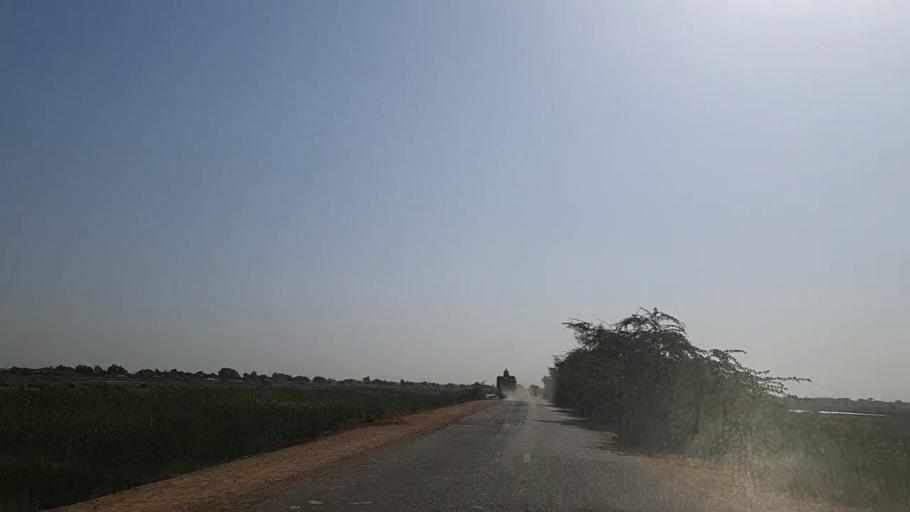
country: PK
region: Sindh
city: Mirpur Batoro
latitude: 24.5820
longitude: 68.2896
